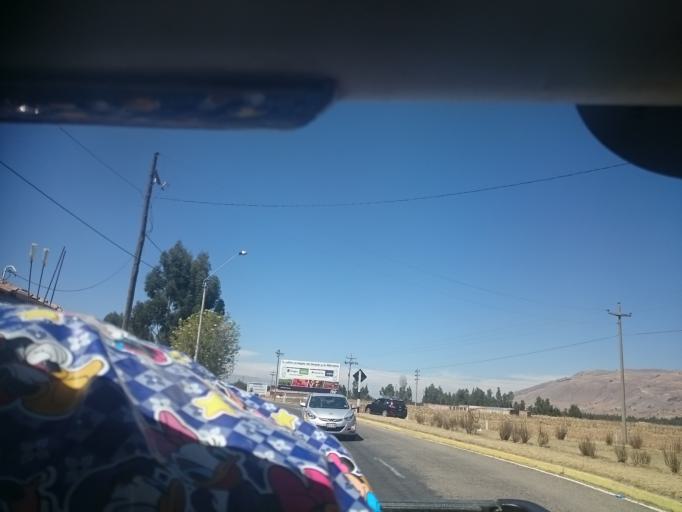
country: PE
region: Junin
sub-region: Provincia de Jauja
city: Sausa
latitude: -11.7868
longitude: -75.4754
